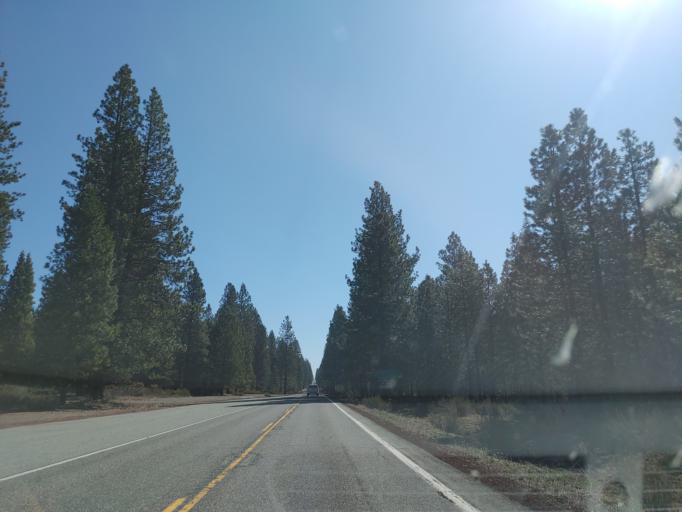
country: US
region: California
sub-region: Siskiyou County
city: McCloud
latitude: 41.2540
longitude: -122.0770
